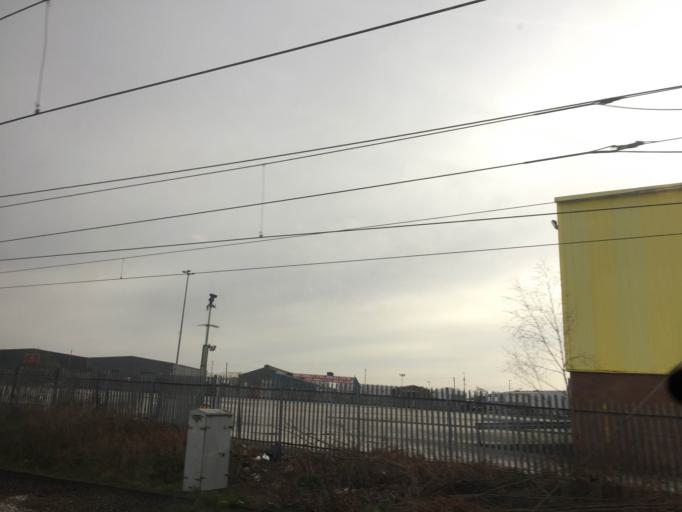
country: GB
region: England
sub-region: Warrington
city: Warrington
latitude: 53.3980
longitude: -2.6003
